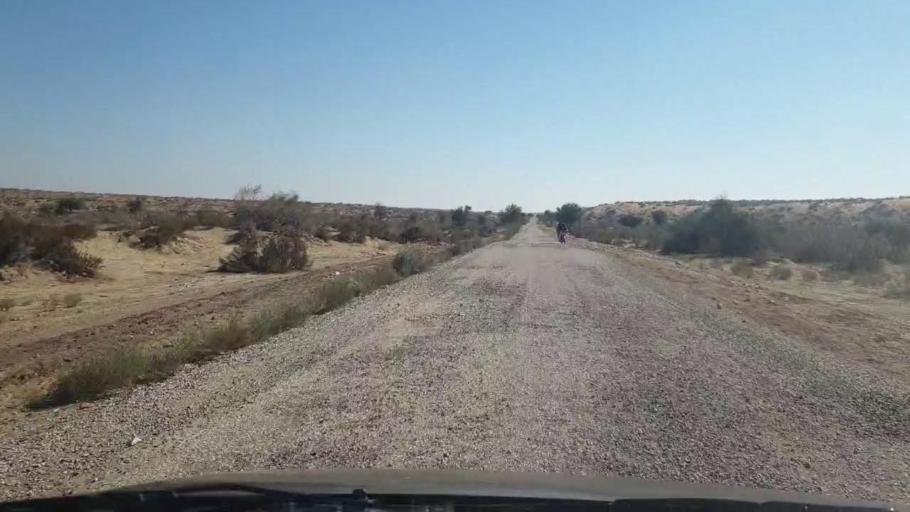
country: PK
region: Sindh
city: Bozdar
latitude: 27.0394
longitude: 68.6913
